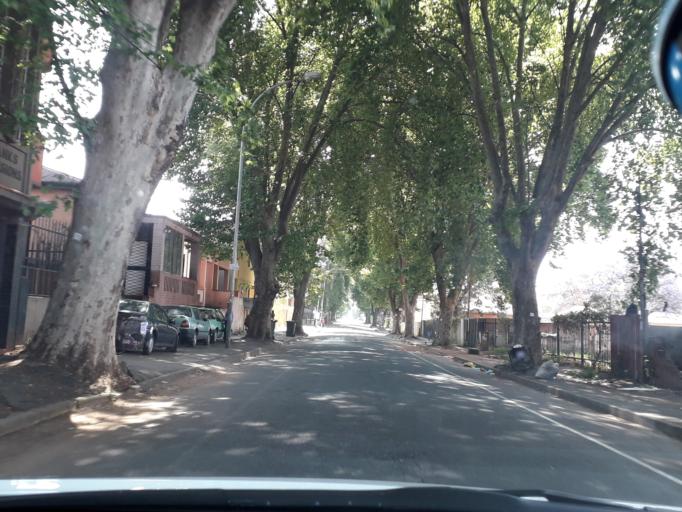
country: ZA
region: Gauteng
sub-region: City of Johannesburg Metropolitan Municipality
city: Johannesburg
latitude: -26.1914
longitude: 28.0638
